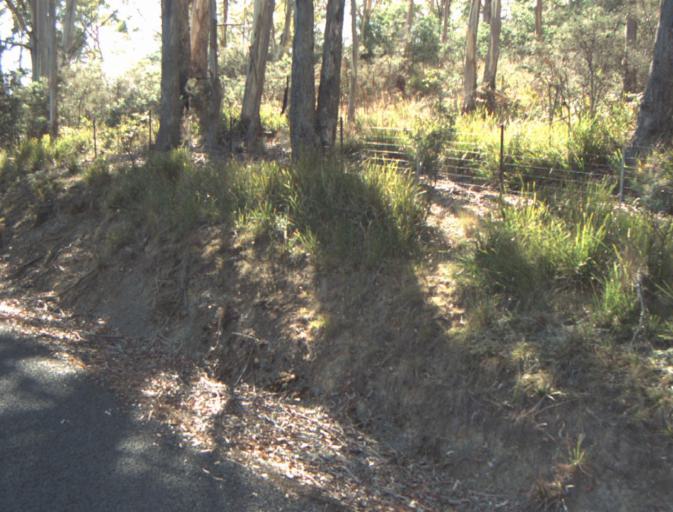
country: AU
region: Tasmania
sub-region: Launceston
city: Newstead
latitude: -41.3682
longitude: 147.3010
